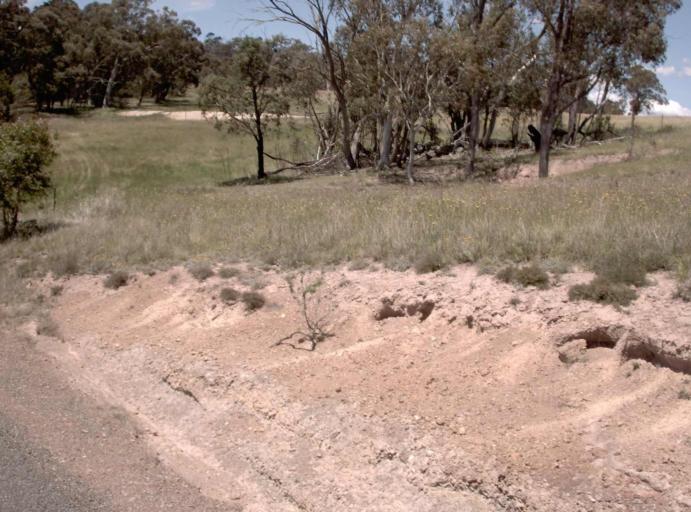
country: AU
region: New South Wales
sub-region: Snowy River
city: Jindabyne
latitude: -37.0792
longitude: 148.2814
